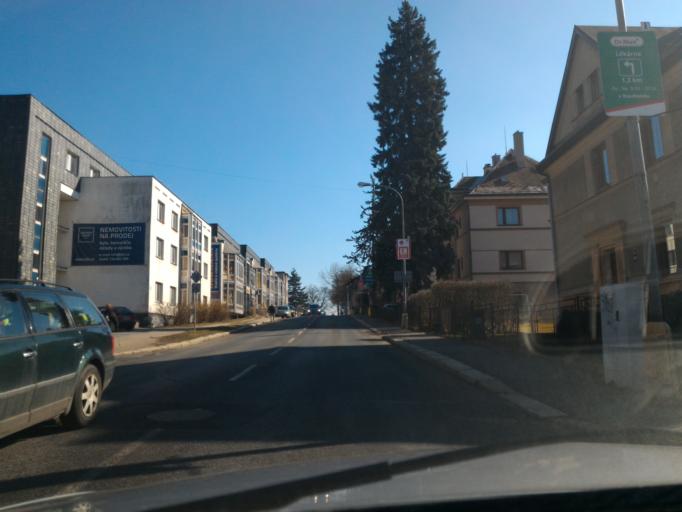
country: CZ
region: Liberecky
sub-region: Okres Jablonec nad Nisou
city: Jablonec nad Nisou
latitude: 50.7320
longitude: 15.1657
